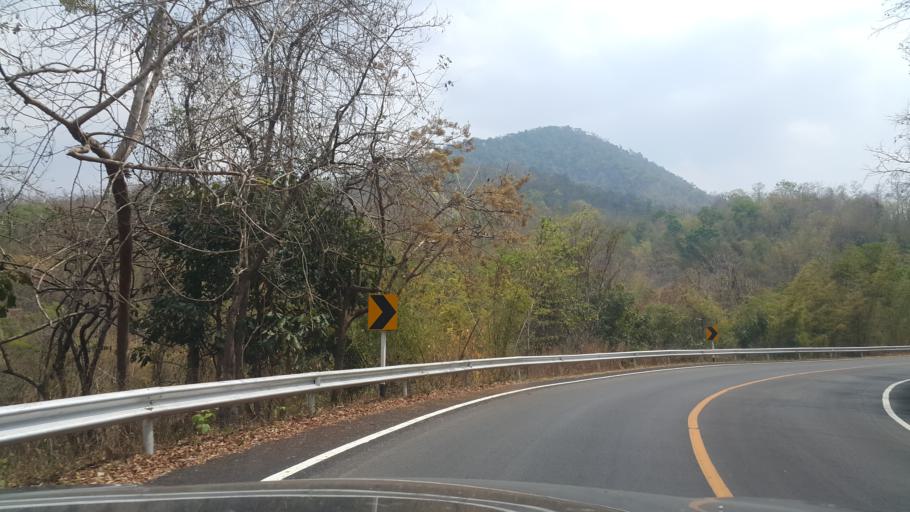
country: TH
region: Lamphun
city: Thung Hua Chang
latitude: 18.1800
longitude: 98.9762
